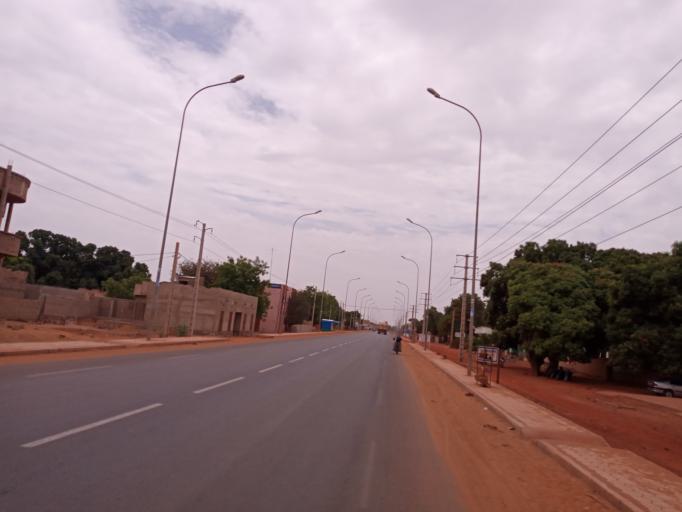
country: ML
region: Koulikoro
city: Koulikoro
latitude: 12.8472
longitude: -7.5780
